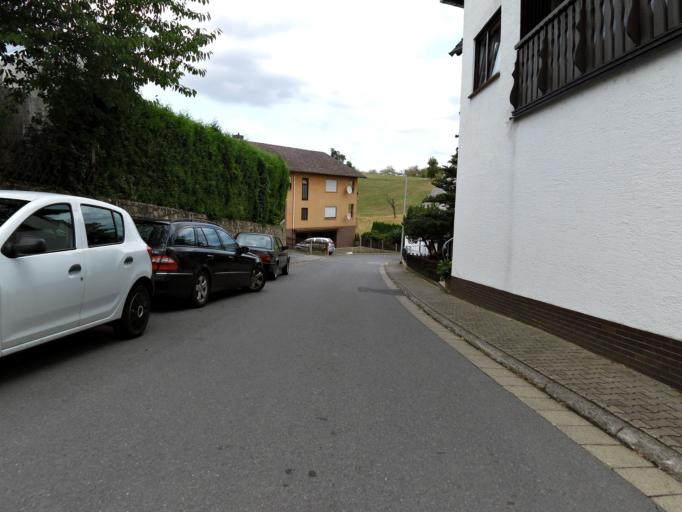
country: DE
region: Hesse
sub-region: Regierungsbezirk Darmstadt
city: Brensbach
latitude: 49.7697
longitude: 8.9318
